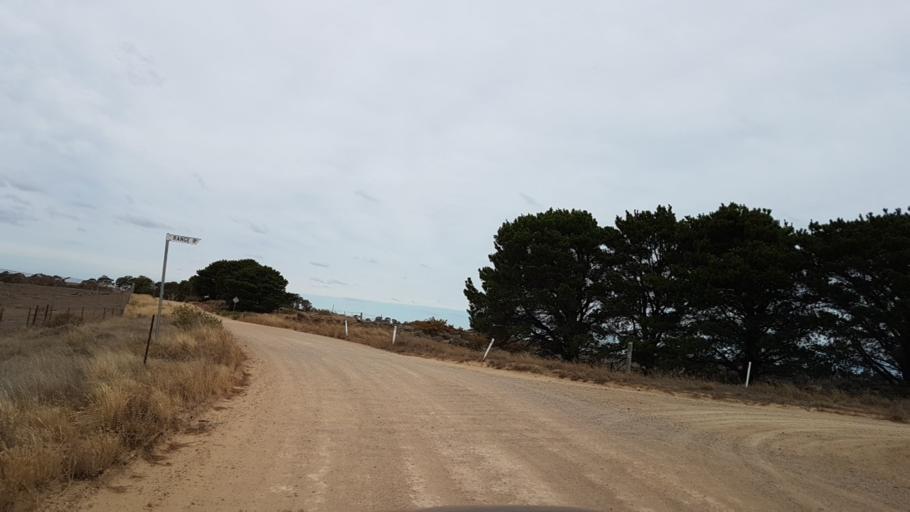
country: AU
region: South Australia
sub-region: Adelaide Hills
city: Birdwood
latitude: -34.8720
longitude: 139.0779
